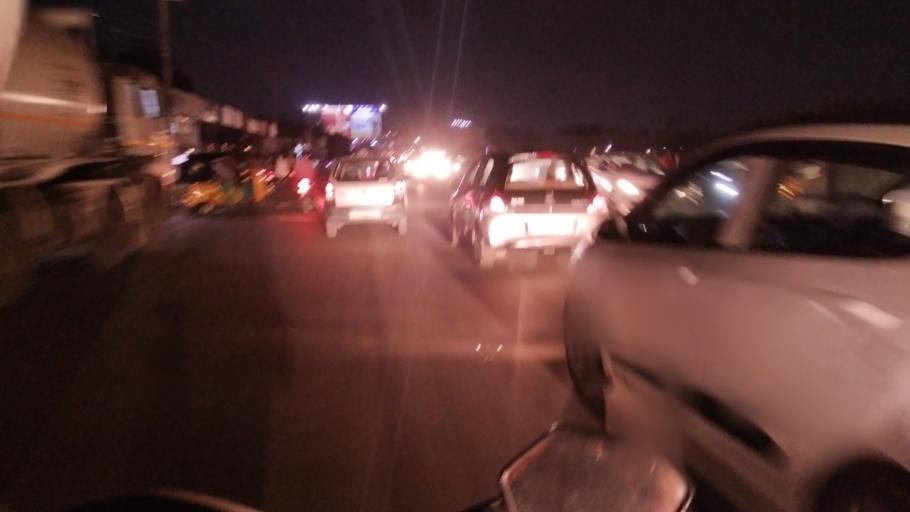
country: IN
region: Telangana
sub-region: Hyderabad
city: Malkajgiri
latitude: 17.4546
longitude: 78.4855
